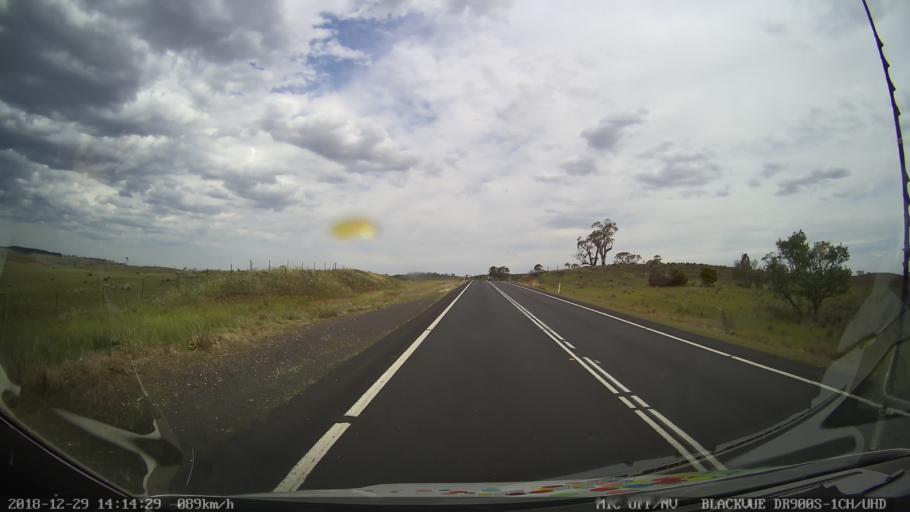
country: AU
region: New South Wales
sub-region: Cooma-Monaro
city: Cooma
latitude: -36.4431
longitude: 149.2374
